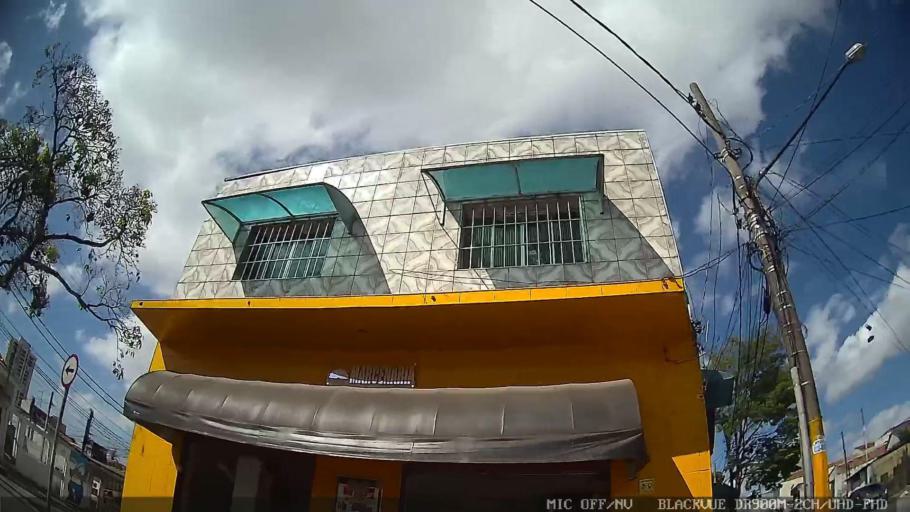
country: BR
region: Sao Paulo
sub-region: Sao Caetano Do Sul
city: Sao Caetano do Sul
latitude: -23.6226
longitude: -46.5943
